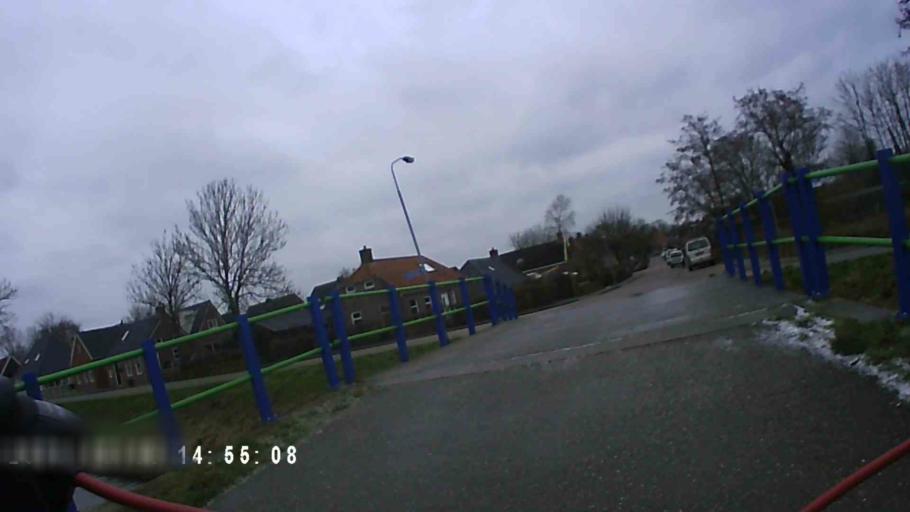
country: NL
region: Groningen
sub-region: Gemeente Winsum
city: Winsum
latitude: 53.3978
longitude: 6.5573
